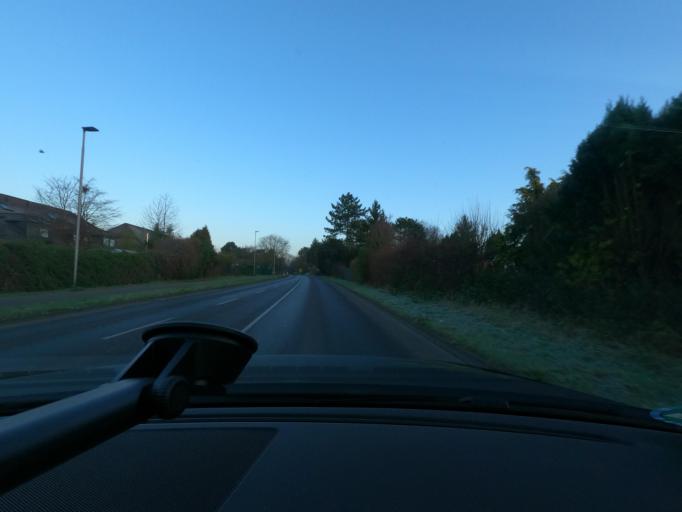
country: DE
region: North Rhine-Westphalia
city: Kempen
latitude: 51.3539
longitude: 6.4135
